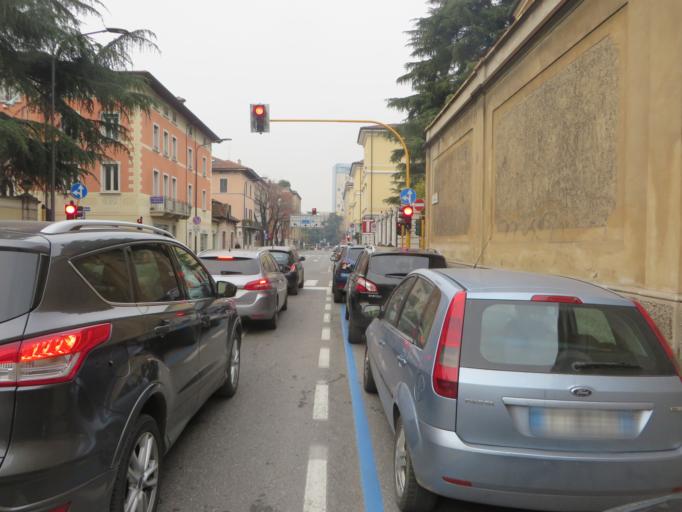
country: IT
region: Lombardy
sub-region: Provincia di Brescia
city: Brescia
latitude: 45.5348
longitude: 10.2151
